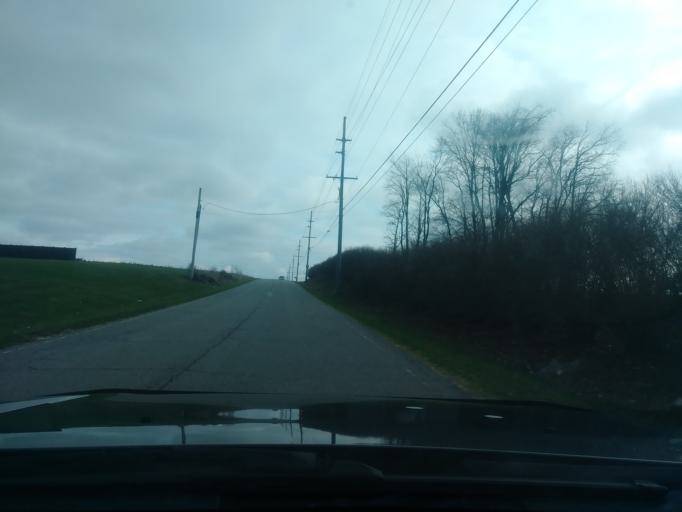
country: US
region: Indiana
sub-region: LaPorte County
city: LaPorte
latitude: 41.6139
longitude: -86.7972
